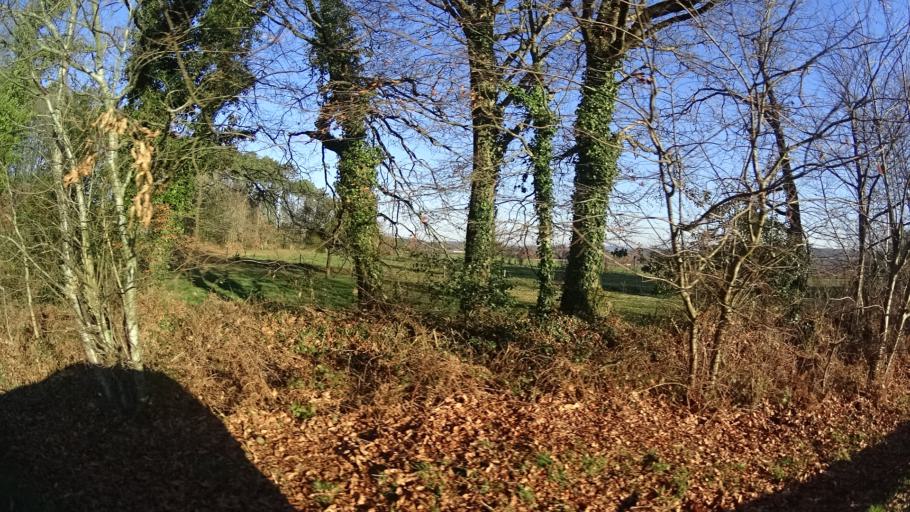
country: FR
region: Brittany
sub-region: Departement du Morbihan
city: Saint-Jacut-les-Pins
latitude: 47.6752
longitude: -2.1823
